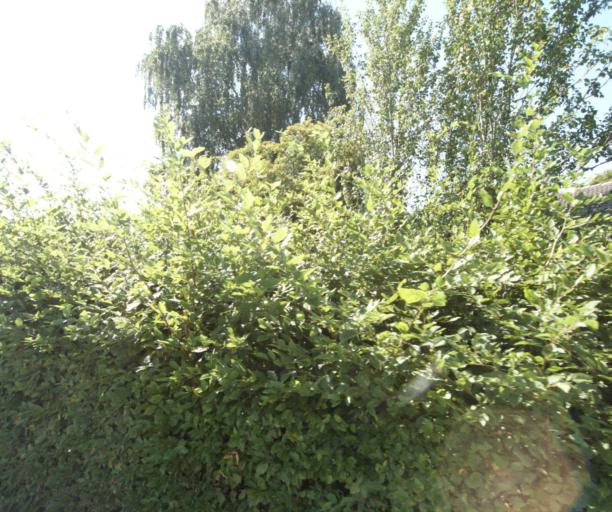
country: FR
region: Nord-Pas-de-Calais
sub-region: Departement du Nord
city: Bousbecque
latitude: 50.7708
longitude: 3.0686
